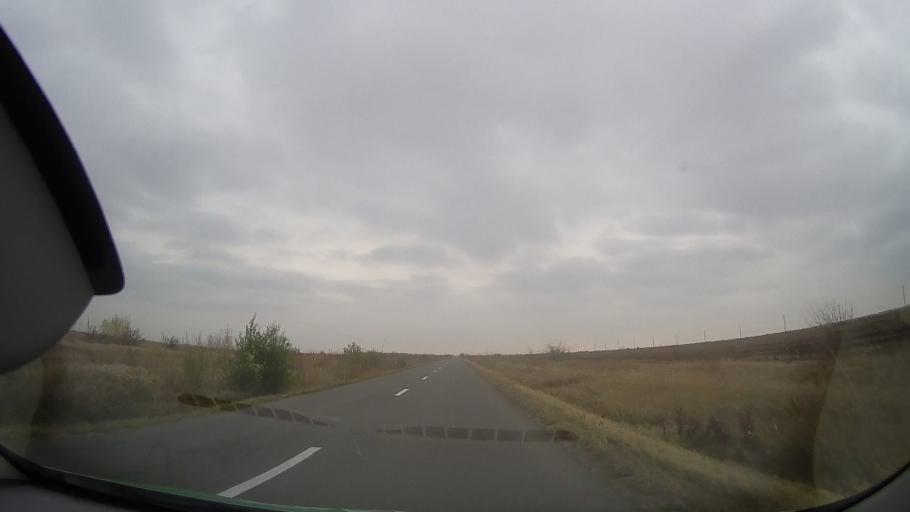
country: RO
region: Ialomita
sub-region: Comuna Garbovi
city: Garbovi
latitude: 44.7561
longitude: 26.7270
